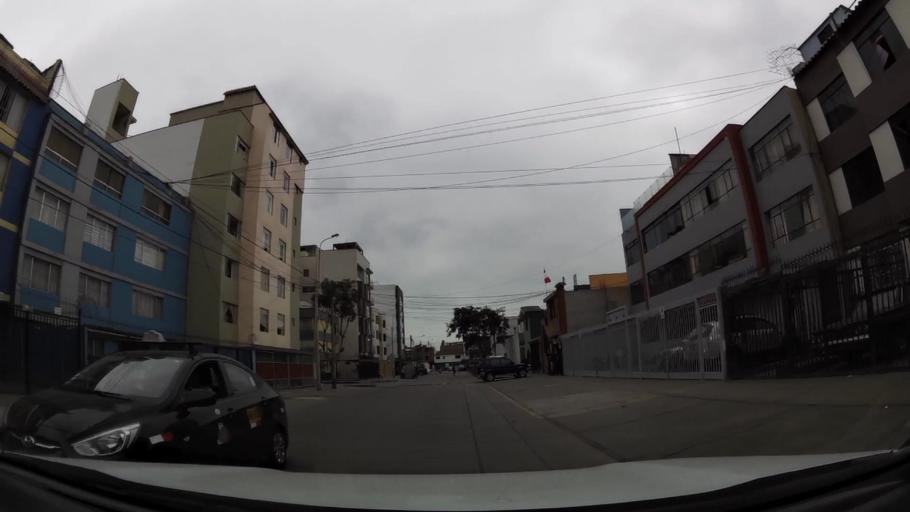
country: PE
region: Lima
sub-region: Lima
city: Surco
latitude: -12.1161
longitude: -77.0151
